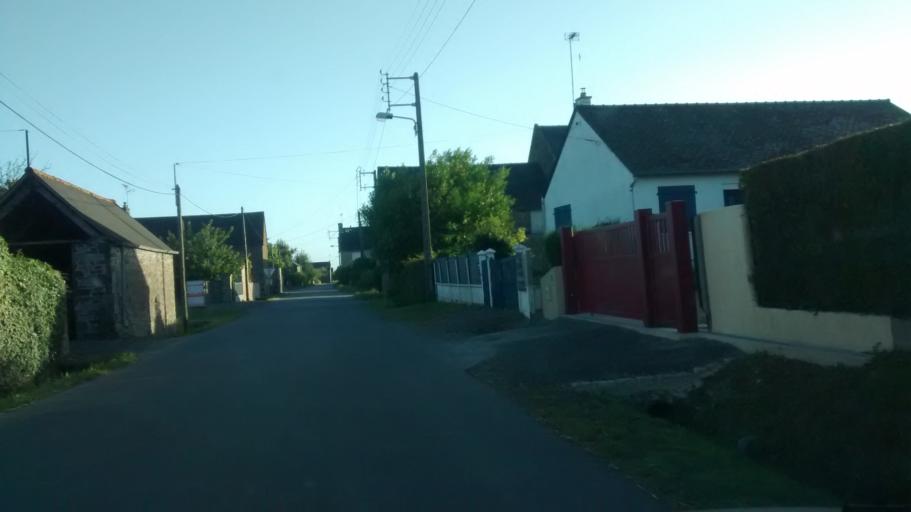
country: FR
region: Brittany
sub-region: Departement d'Ille-et-Vilaine
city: La Fresnais
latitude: 48.5909
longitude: -1.8581
